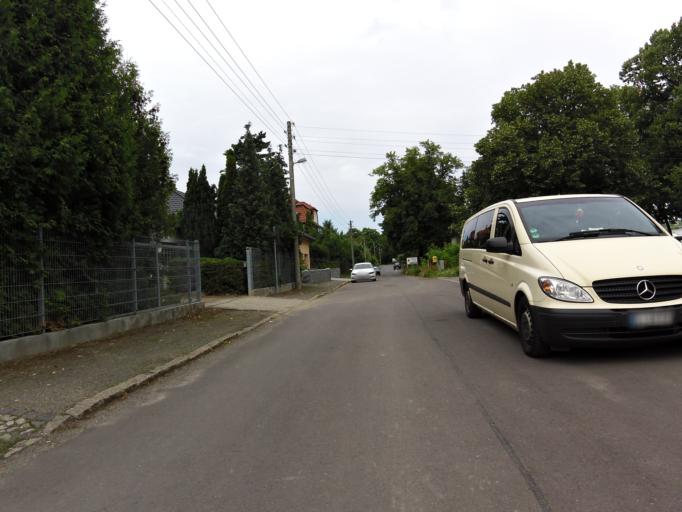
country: DE
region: Saxony
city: Rackwitz
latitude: 51.3995
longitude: 12.3864
